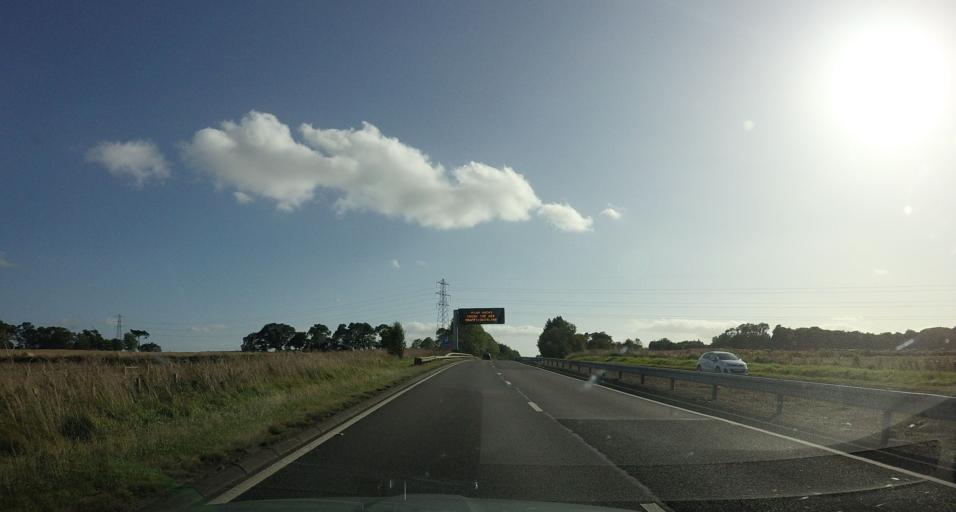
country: GB
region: Scotland
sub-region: Dundee City
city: Dundee
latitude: 56.5073
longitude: -2.9456
